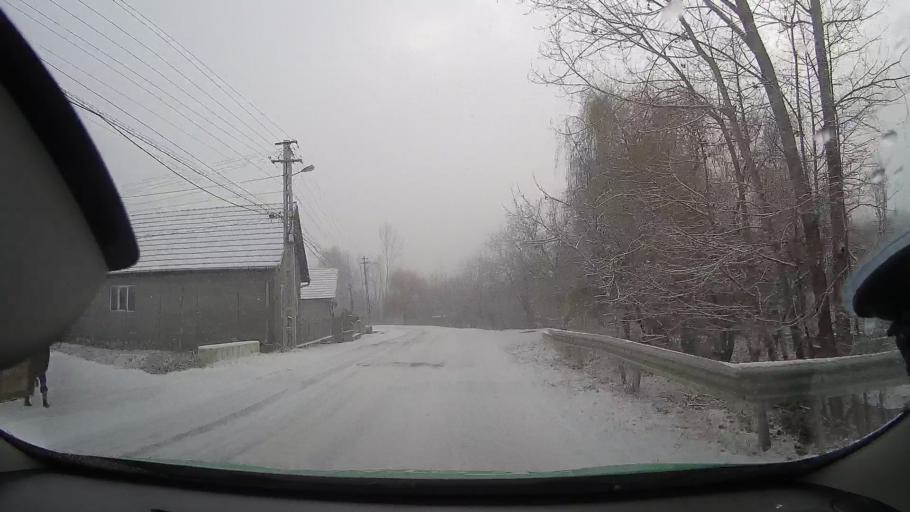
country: RO
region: Alba
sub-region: Comuna Livezile
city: Livezile
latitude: 46.3436
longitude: 23.6588
